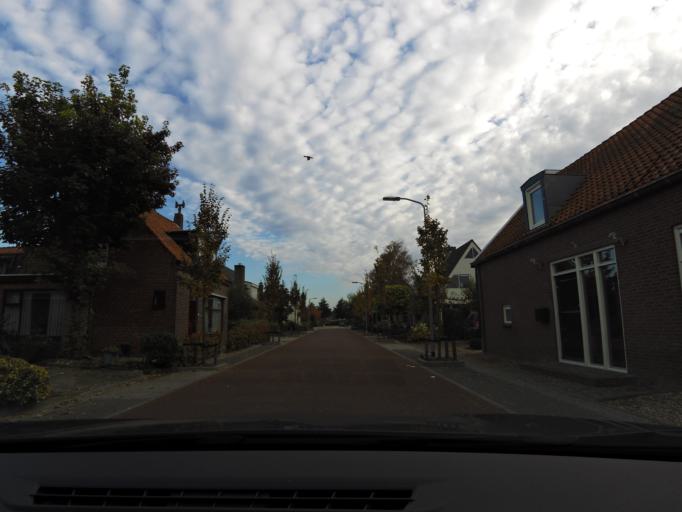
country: NL
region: South Holland
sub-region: Gemeente Goeree-Overflakkee
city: Middelharnis
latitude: 51.7147
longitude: 4.1707
